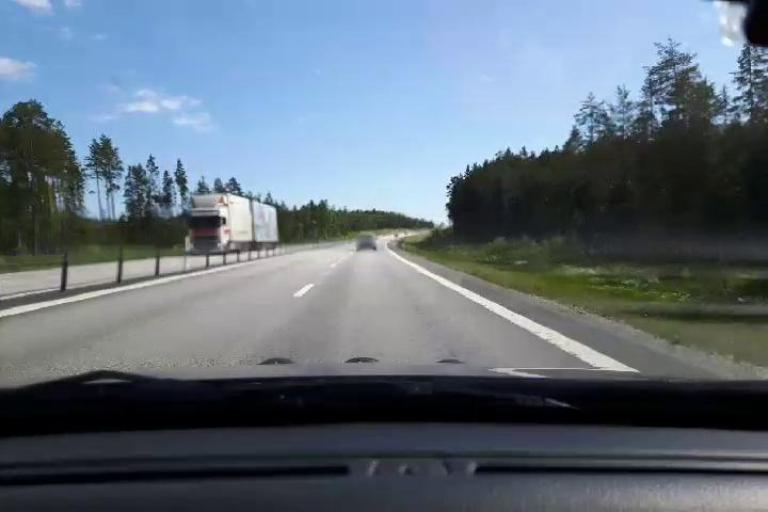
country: SE
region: Gaevleborg
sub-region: Hudiksvalls Kommun
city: Hudiksvall
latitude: 61.6998
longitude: 17.0554
